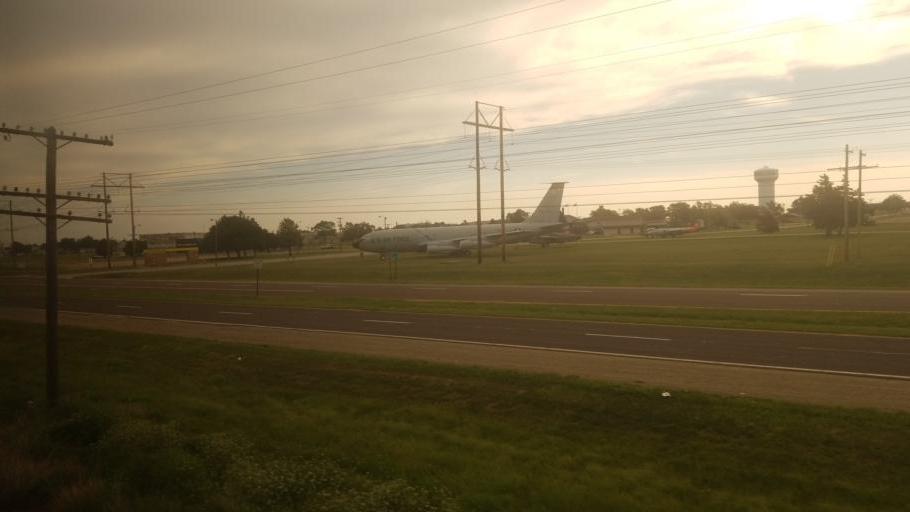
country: US
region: Kansas
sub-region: Shawnee County
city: Topeka
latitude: 38.9454
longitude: -95.6876
